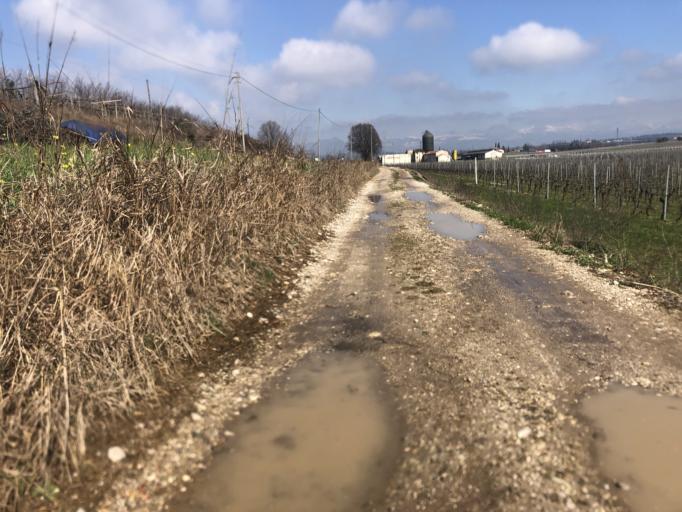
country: IT
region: Veneto
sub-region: Provincia di Verona
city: San Giorgio in Salici
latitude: 45.4114
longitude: 10.7919
